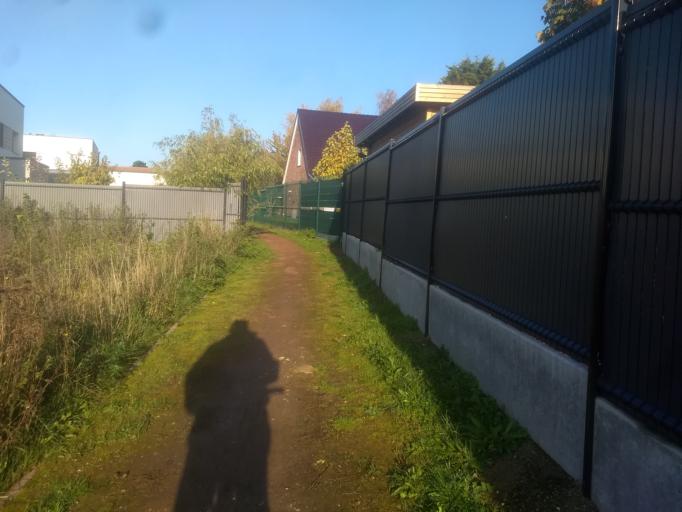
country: FR
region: Nord-Pas-de-Calais
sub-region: Departement du Pas-de-Calais
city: Tilloy-les-Mofflaines
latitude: 50.2780
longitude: 2.8180
